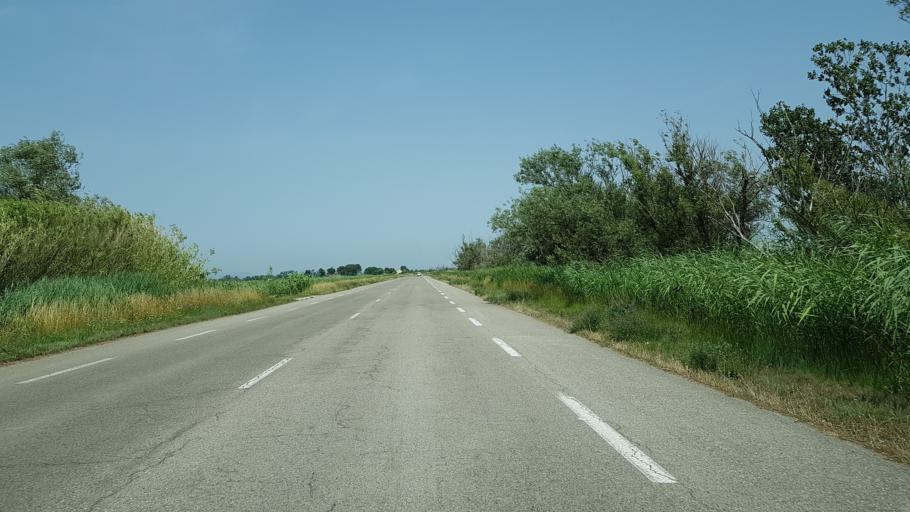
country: FR
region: Provence-Alpes-Cote d'Azur
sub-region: Departement des Bouches-du-Rhone
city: Port-Saint-Louis-du-Rhone
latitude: 43.4633
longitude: 4.7589
